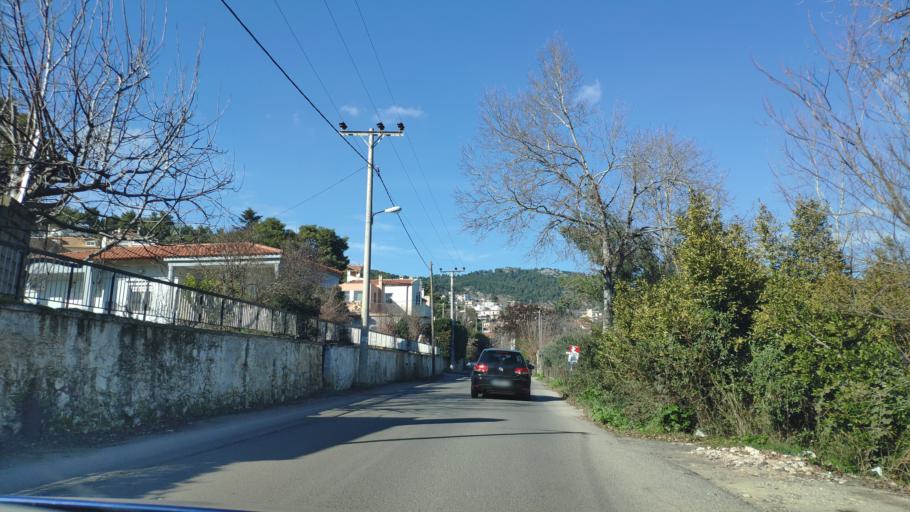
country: GR
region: Attica
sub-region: Nomarchia Anatolikis Attikis
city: Afidnes
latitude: 38.1998
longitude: 23.8408
